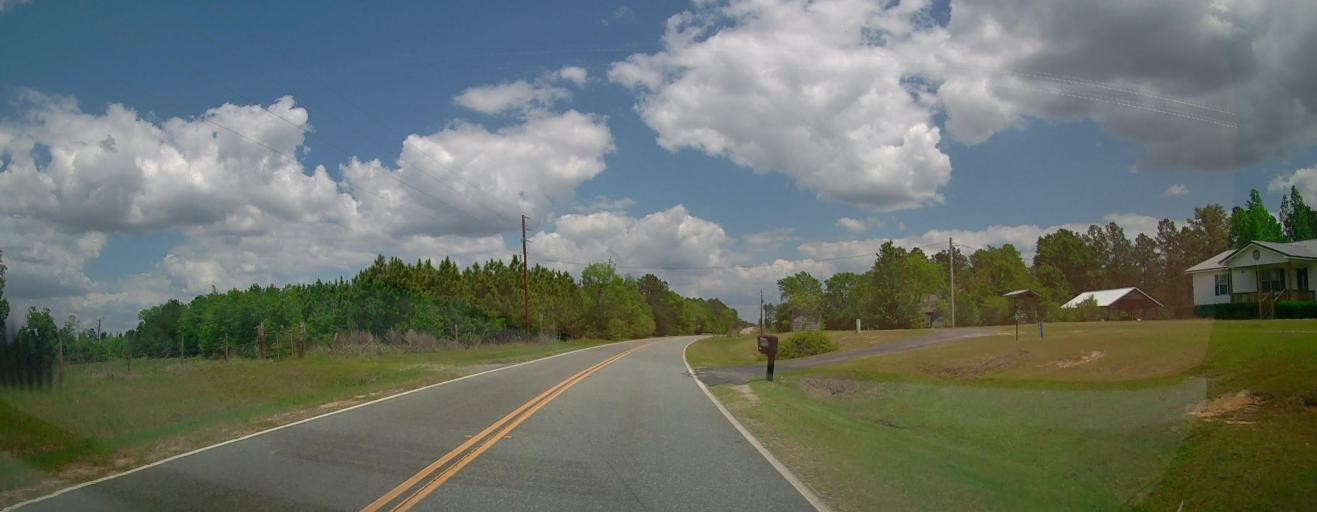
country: US
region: Georgia
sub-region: Laurens County
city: East Dublin
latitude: 32.5276
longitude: -82.7102
